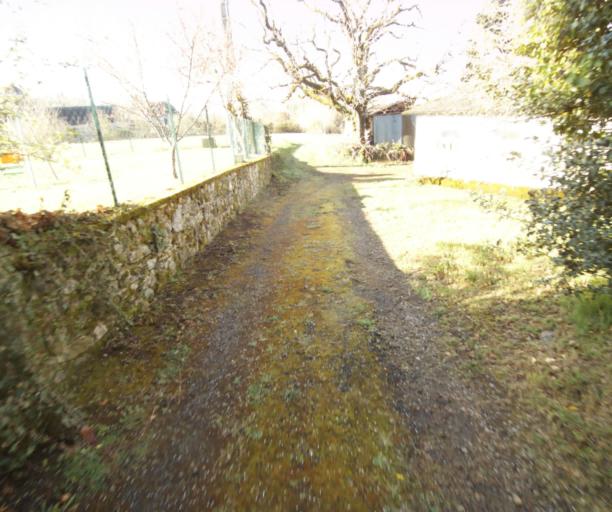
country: FR
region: Limousin
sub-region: Departement de la Correze
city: Laguenne
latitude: 45.2842
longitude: 1.8533
